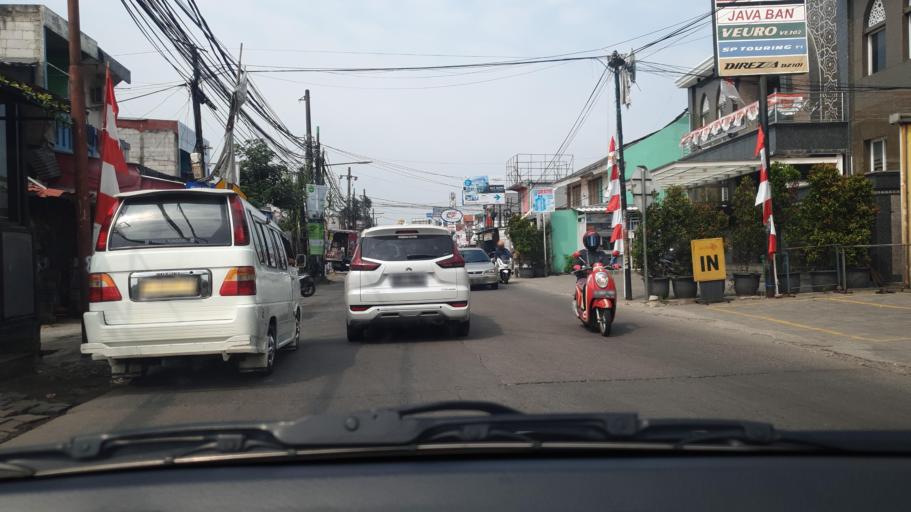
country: ID
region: West Java
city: Pamulang
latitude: -6.3151
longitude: 106.7695
